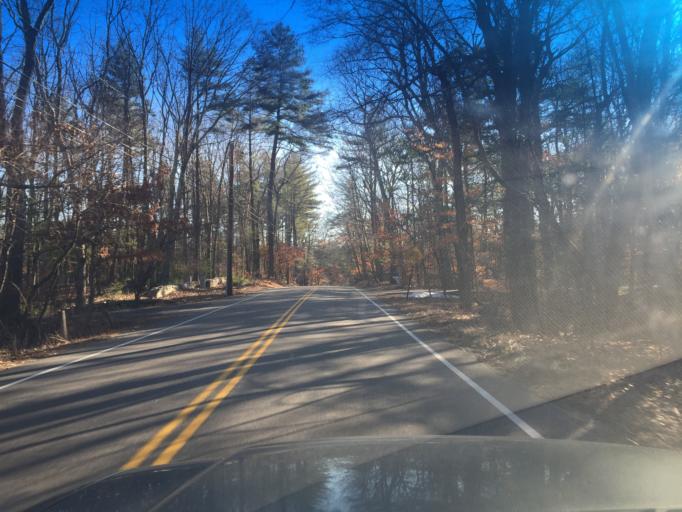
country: US
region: Massachusetts
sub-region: Norfolk County
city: Millis
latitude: 42.1912
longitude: -71.3783
